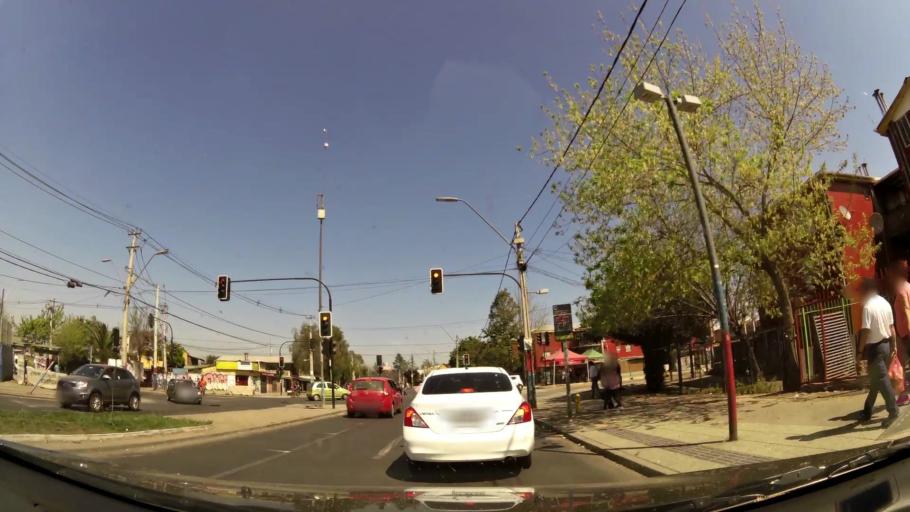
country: CL
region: Santiago Metropolitan
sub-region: Provincia de Santiago
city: Lo Prado
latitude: -33.4054
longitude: -70.7455
